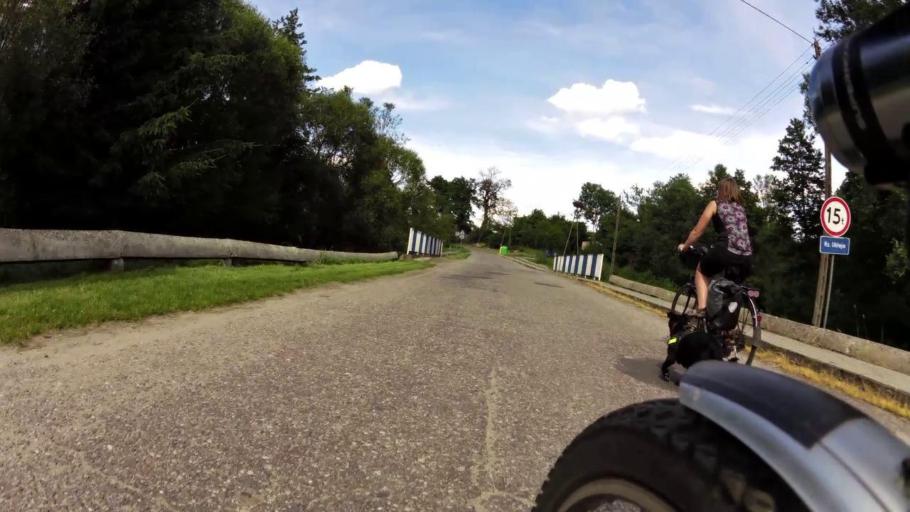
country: PL
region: West Pomeranian Voivodeship
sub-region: Powiat lobeski
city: Dobra
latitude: 53.5836
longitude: 15.3973
